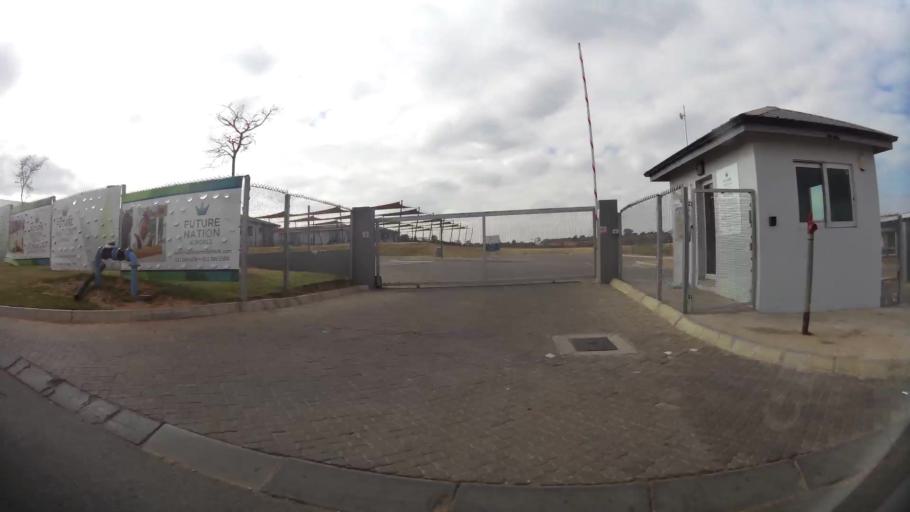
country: ZA
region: Gauteng
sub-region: City of Johannesburg Metropolitan Municipality
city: Roodepoort
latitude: -26.2078
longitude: 27.9149
